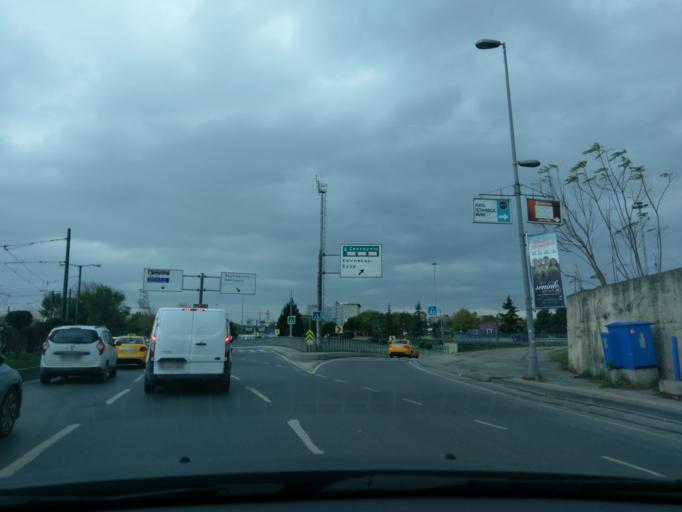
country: TR
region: Istanbul
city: Istanbul
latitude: 41.0197
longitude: 28.9246
